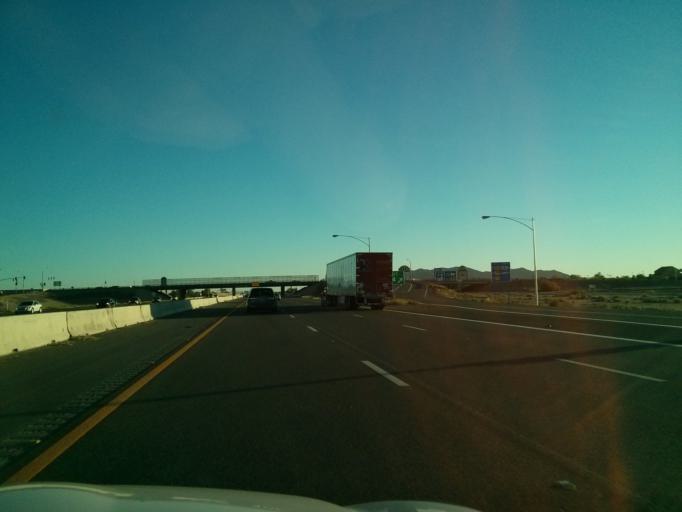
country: US
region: Arizona
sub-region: Pinal County
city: Casa Grande
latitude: 32.8824
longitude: -111.6870
